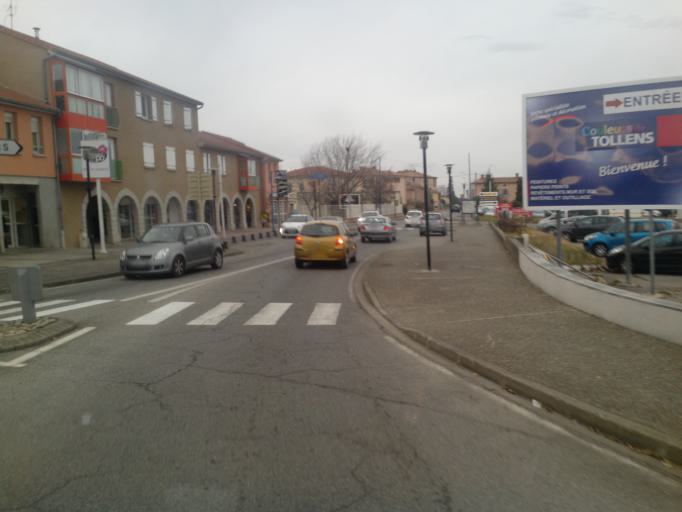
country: FR
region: Midi-Pyrenees
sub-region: Departement de l'Ariege
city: Saint-Jean-du-Falga
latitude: 43.0860
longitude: 1.6284
